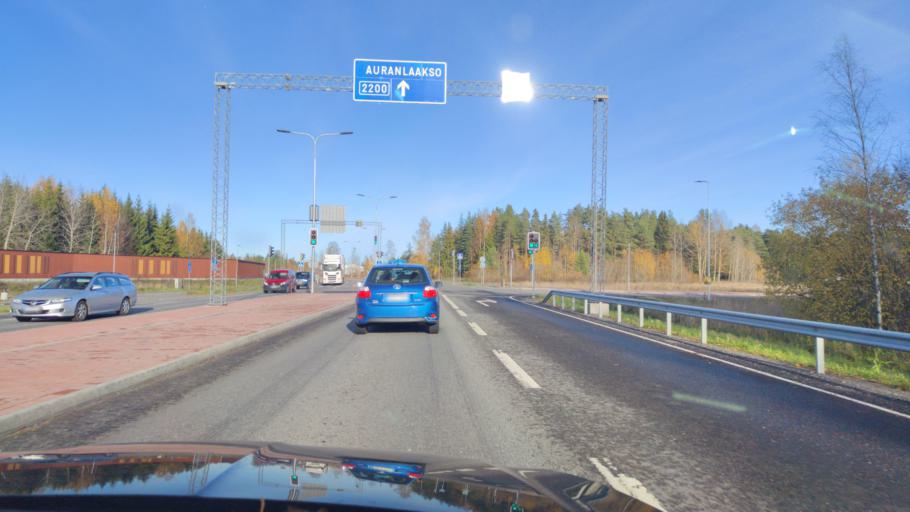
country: FI
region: Varsinais-Suomi
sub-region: Turku
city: Kaarina
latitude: 60.4277
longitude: 22.3826
